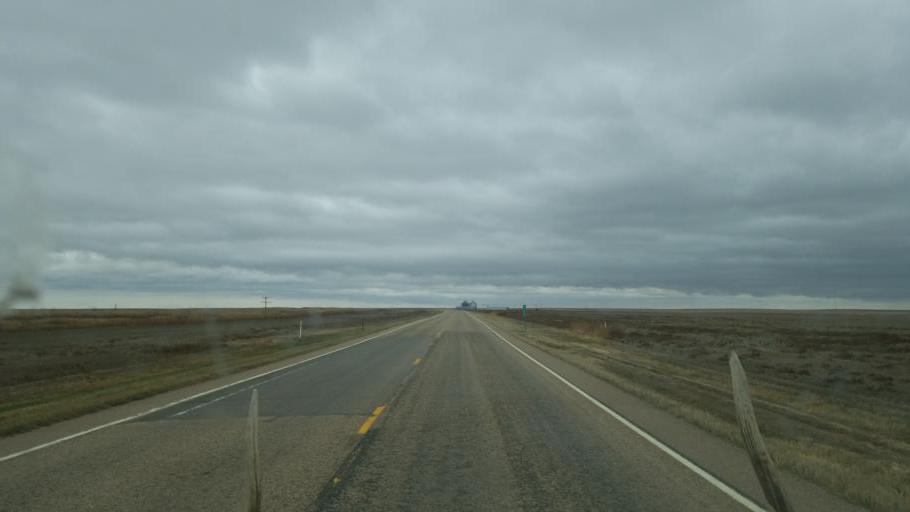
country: US
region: Colorado
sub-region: Cheyenne County
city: Cheyenne Wells
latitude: 38.8053
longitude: -102.6050
